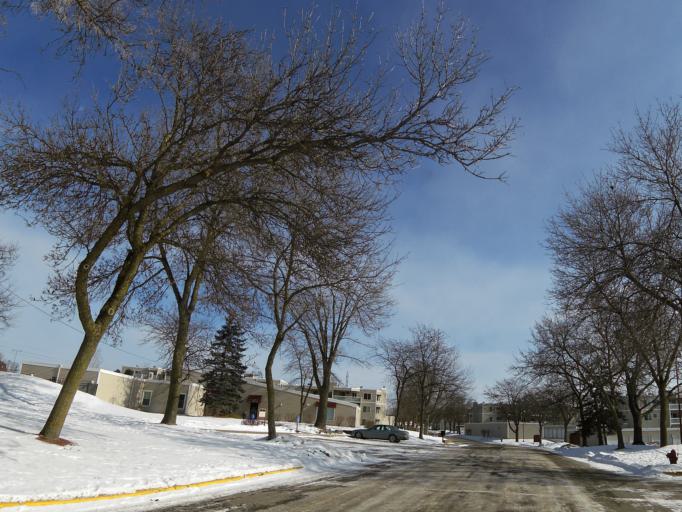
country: US
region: Minnesota
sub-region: Washington County
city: Oakdale
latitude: 44.9474
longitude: -92.9689
